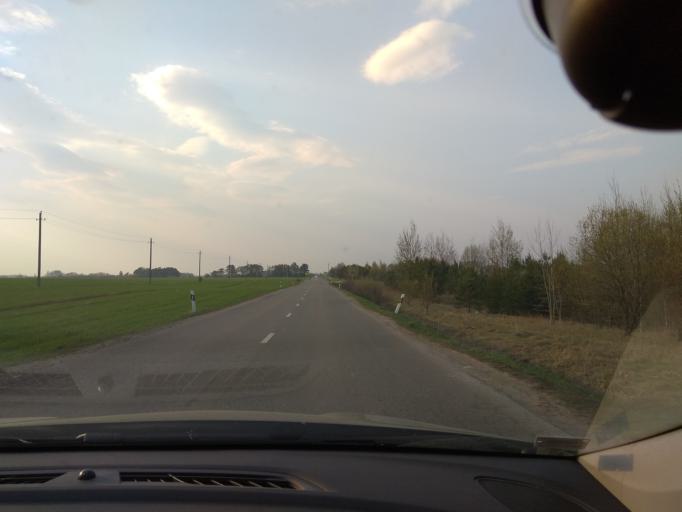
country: LT
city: Grigiskes
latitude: 54.6153
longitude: 25.1183
